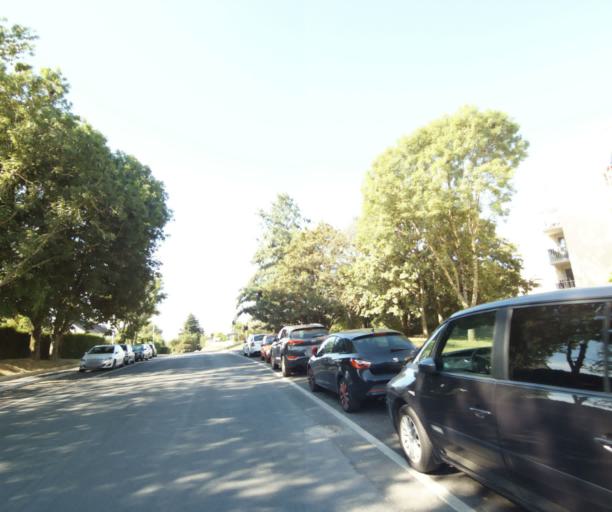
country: FR
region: Ile-de-France
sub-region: Departement de Seine-et-Marne
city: Gouvernes
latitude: 48.8667
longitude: 2.6987
